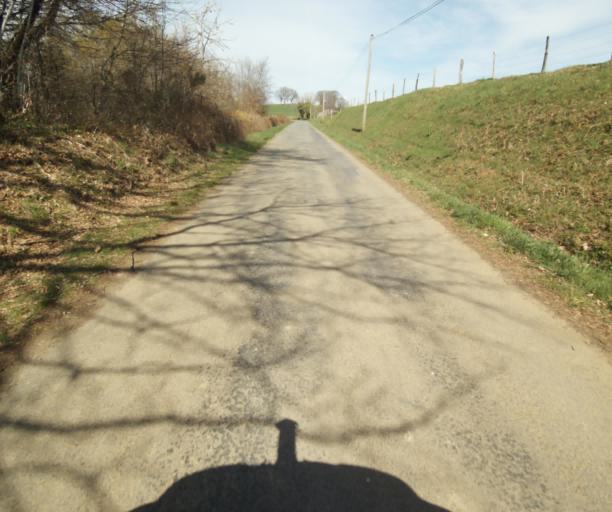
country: FR
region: Limousin
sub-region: Departement de la Correze
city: Seilhac
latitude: 45.3929
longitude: 1.7830
